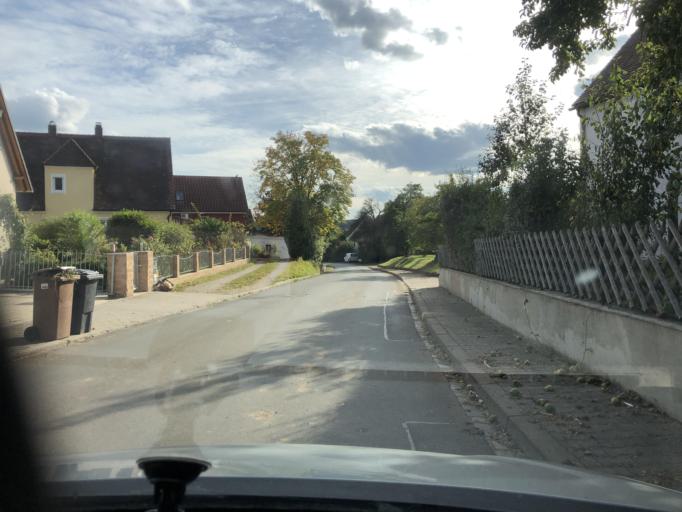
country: DE
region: Bavaria
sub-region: Regierungsbezirk Mittelfranken
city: Cadolzburg
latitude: 49.4748
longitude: 10.8251
